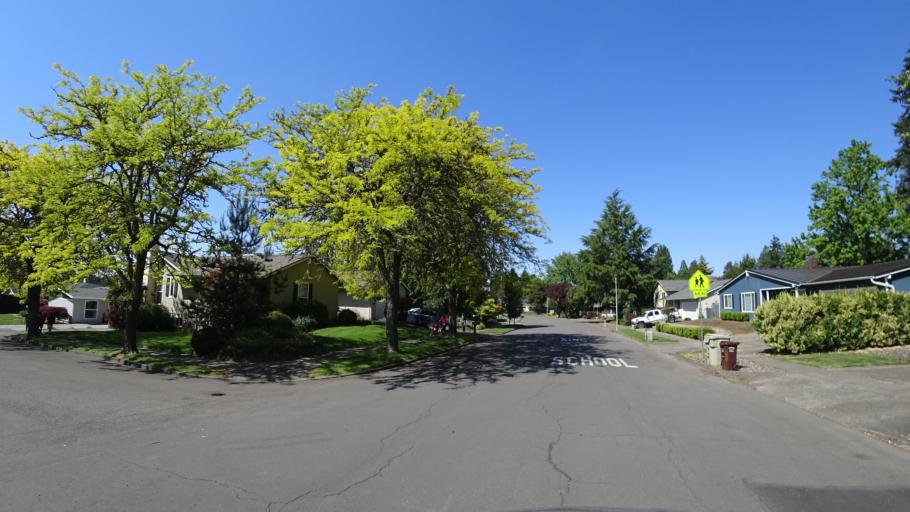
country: US
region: Oregon
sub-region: Washington County
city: Rockcreek
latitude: 45.5511
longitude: -122.8715
